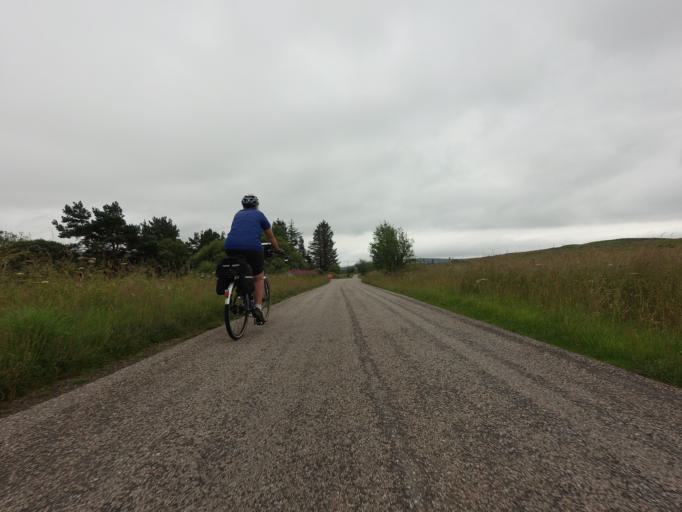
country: GB
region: Scotland
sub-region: Highland
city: Alness
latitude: 58.0099
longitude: -4.4031
